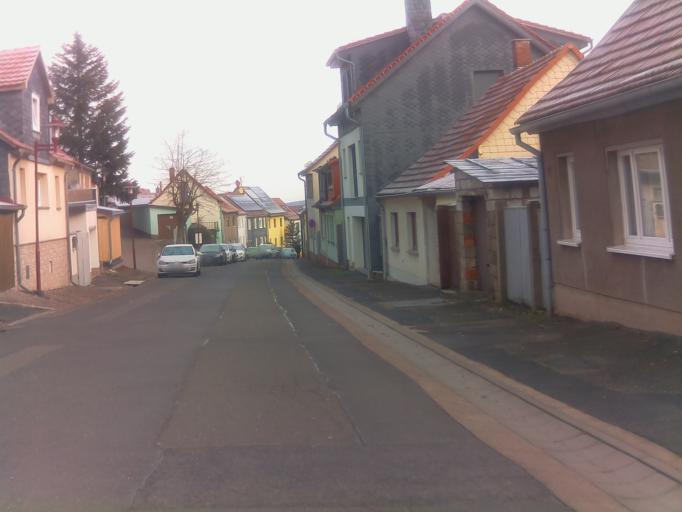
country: DE
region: Thuringia
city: Grafenhain
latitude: 50.8141
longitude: 10.6941
